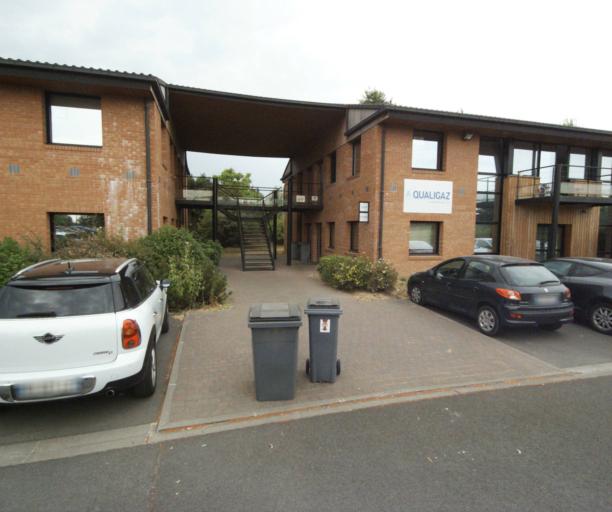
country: FR
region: Nord-Pas-de-Calais
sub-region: Departement du Nord
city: Marquette-lez-Lille
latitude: 50.6846
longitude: 3.0628
